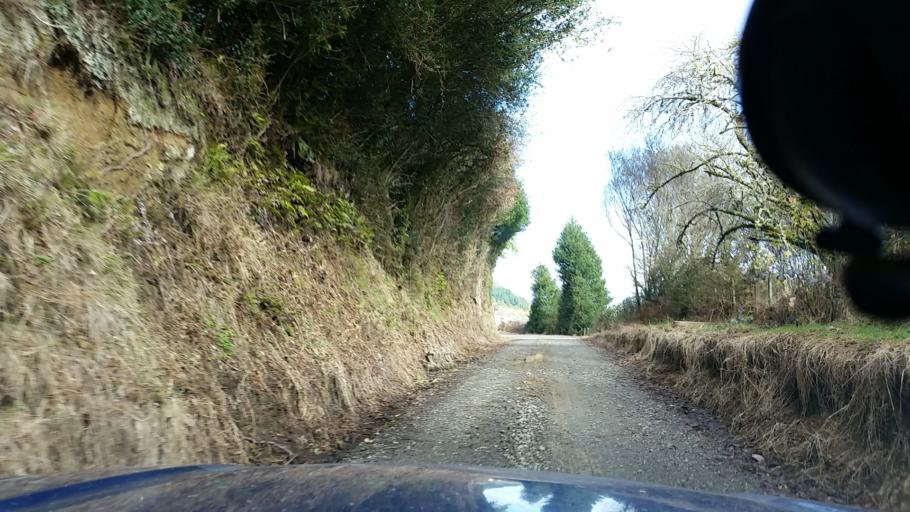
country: NZ
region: Taranaki
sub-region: New Plymouth District
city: Waitara
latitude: -39.0321
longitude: 174.8014
